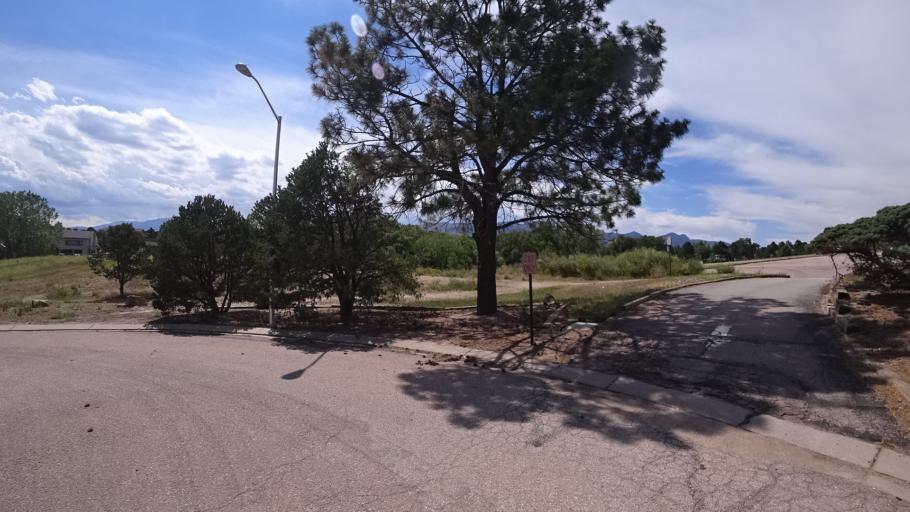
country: US
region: Colorado
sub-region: El Paso County
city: Air Force Academy
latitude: 38.9320
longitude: -104.8307
